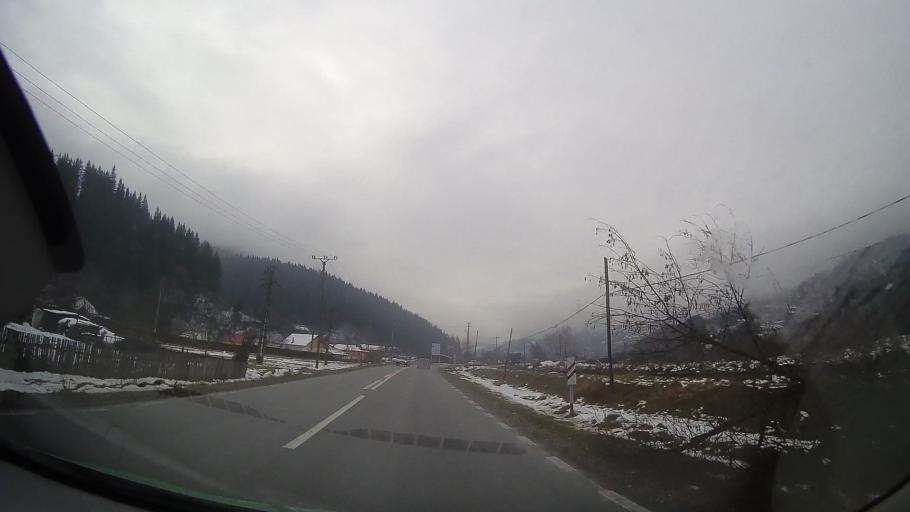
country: RO
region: Neamt
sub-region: Comuna Tasca
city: Tasca
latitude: 46.8792
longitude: 25.9870
